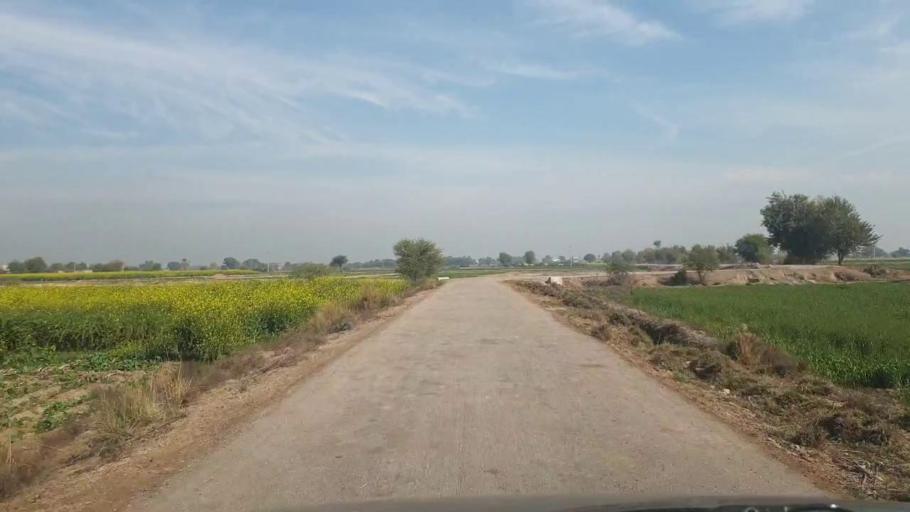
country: PK
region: Sindh
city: Shahpur Chakar
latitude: 26.1812
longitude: 68.5799
